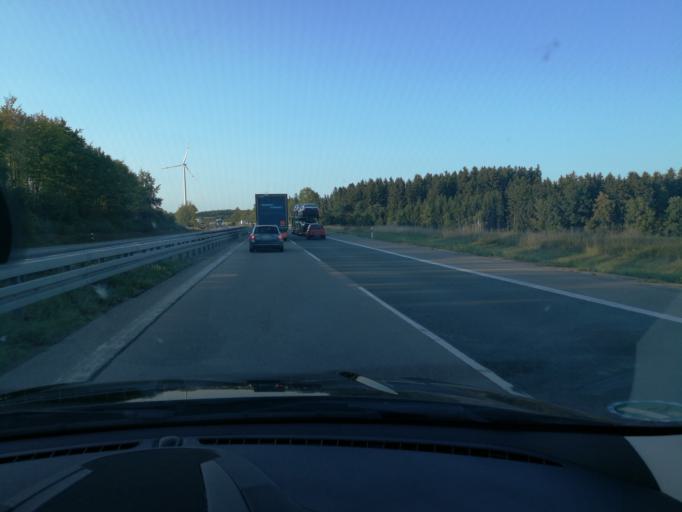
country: DE
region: Bavaria
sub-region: Upper Palatinate
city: Pilsach
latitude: 49.3029
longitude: 11.5500
